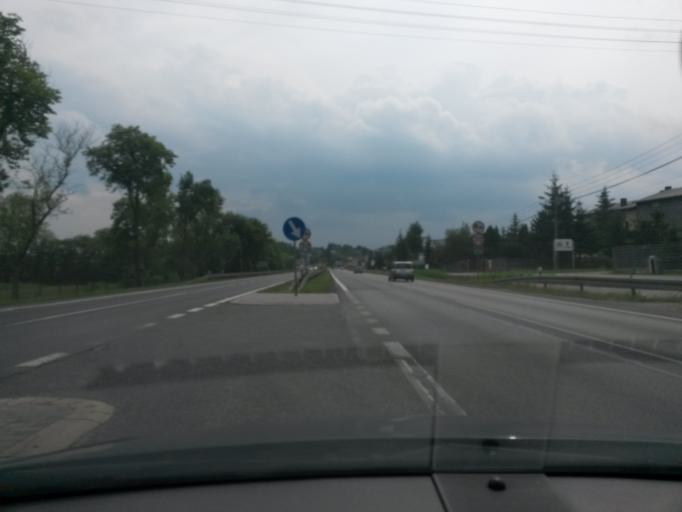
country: PL
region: Silesian Voivodeship
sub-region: Powiat czestochowski
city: Huta Stara B
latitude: 50.7550
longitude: 19.1552
